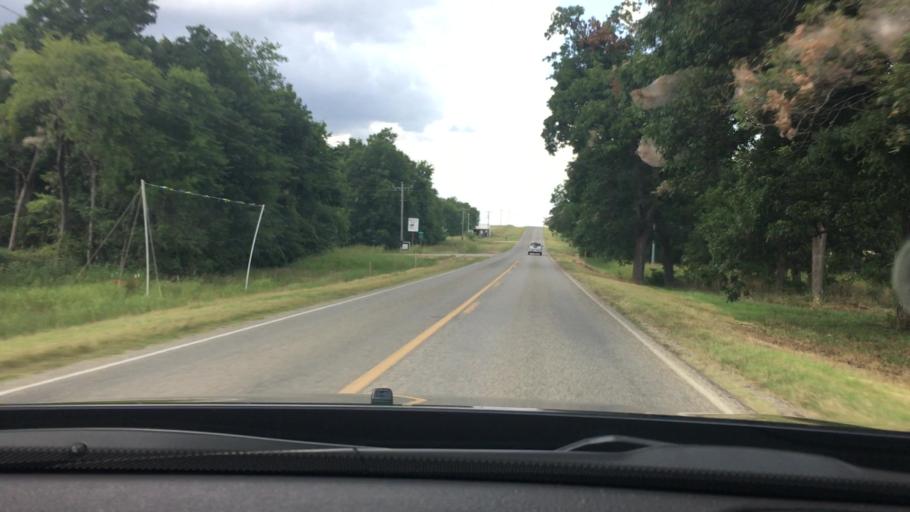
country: US
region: Oklahoma
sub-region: Pontotoc County
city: Ada
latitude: 34.5481
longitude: -96.6347
